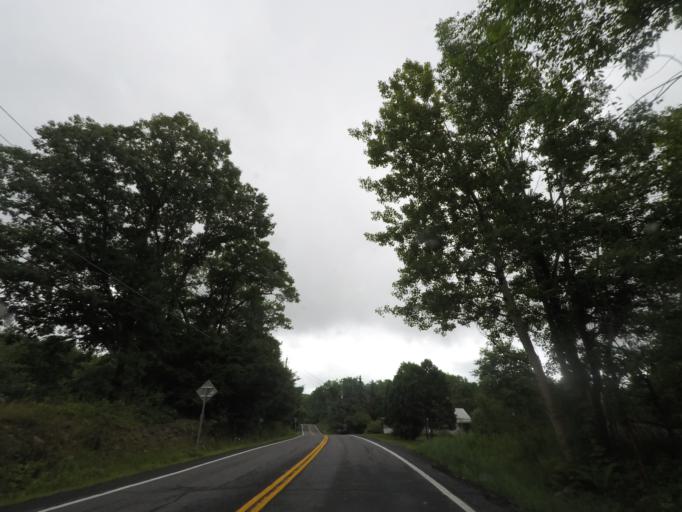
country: US
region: New York
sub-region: Rensselaer County
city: Averill Park
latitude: 42.5835
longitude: -73.4835
